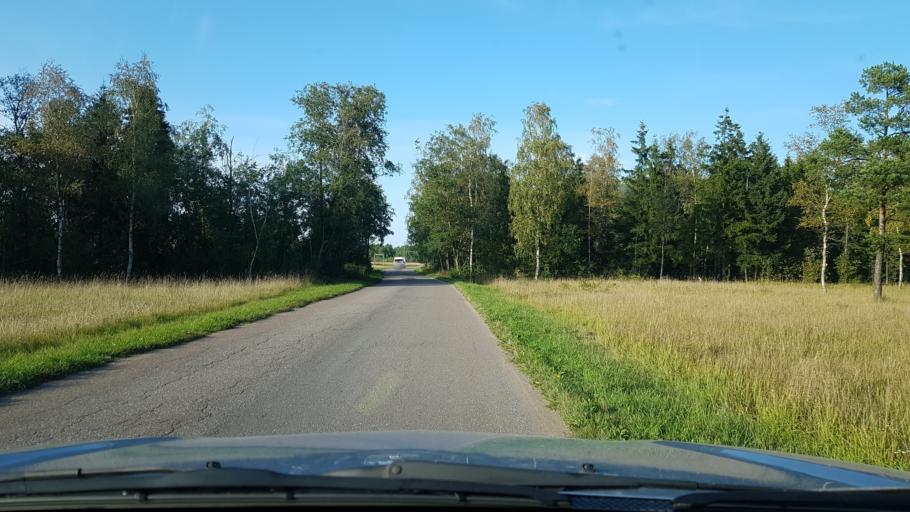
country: EE
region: Ida-Virumaa
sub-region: Narva-Joesuu linn
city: Narva-Joesuu
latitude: 59.3846
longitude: 28.0879
